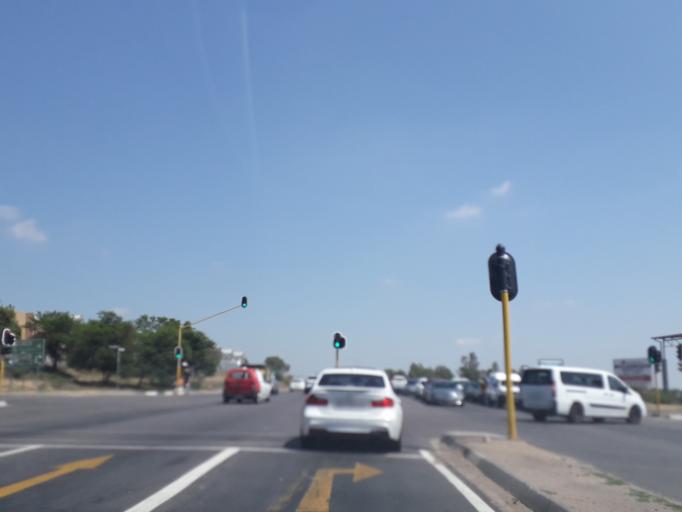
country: ZA
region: Gauteng
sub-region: West Rand District Municipality
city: Muldersdriseloop
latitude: -26.0286
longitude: 27.9455
